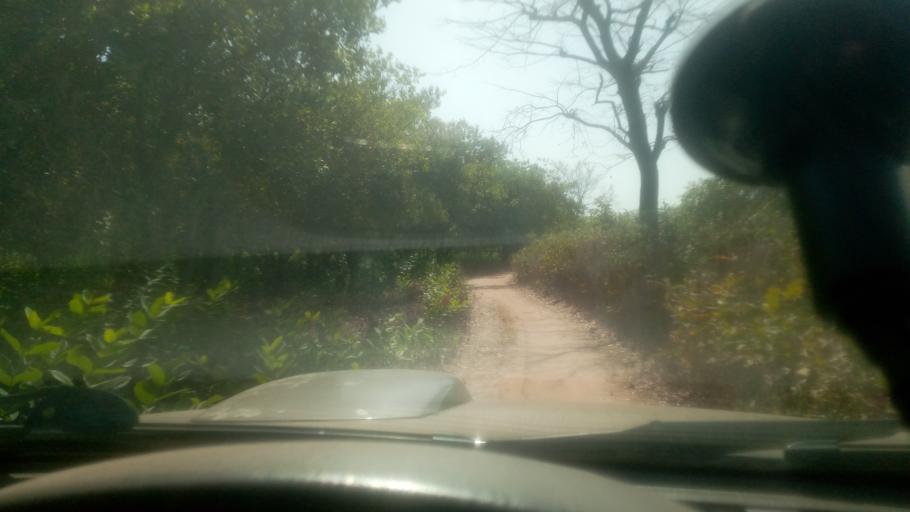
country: GW
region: Oio
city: Farim
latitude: 12.4537
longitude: -15.4131
